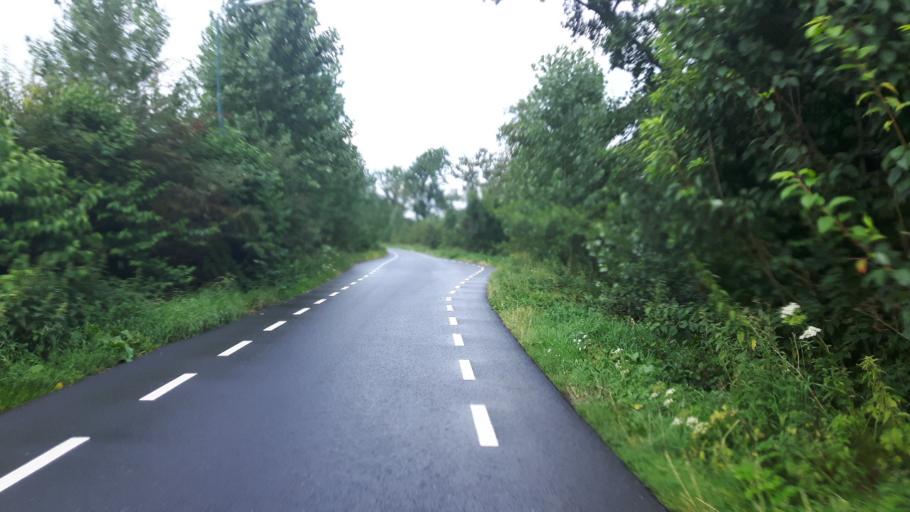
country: NL
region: Utrecht
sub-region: Gemeente Oudewater
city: Oudewater
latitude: 52.0271
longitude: 4.9052
